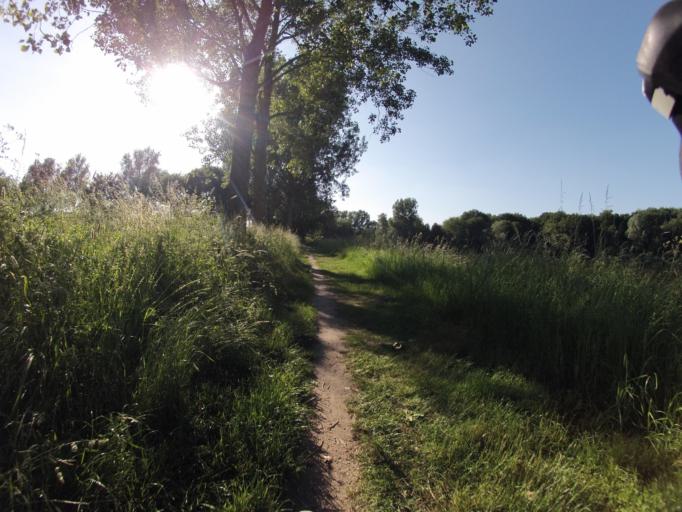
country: DE
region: Lower Saxony
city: Schuttorf
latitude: 52.3168
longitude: 7.2351
